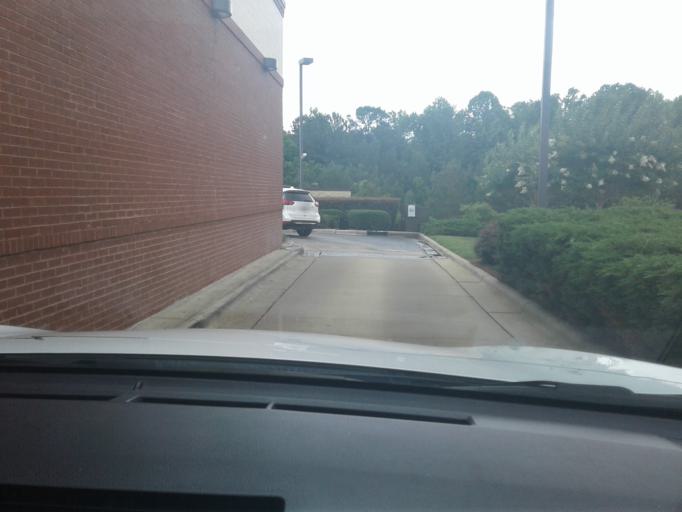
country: US
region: North Carolina
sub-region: Wake County
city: Fuquay-Varina
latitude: 35.5938
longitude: -78.7679
